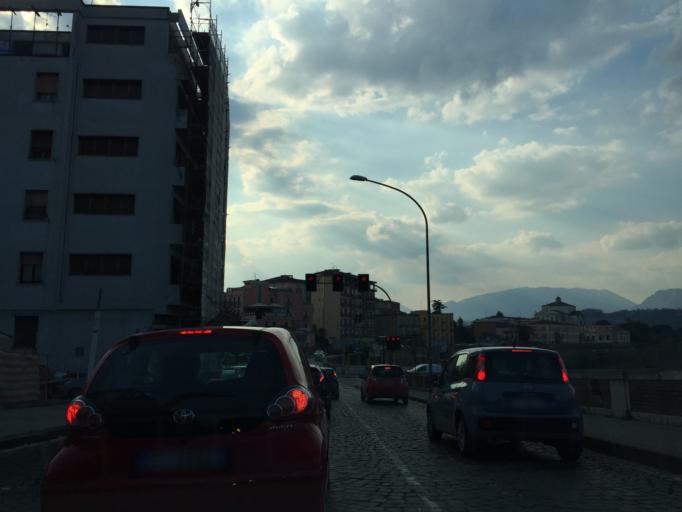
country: IT
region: Campania
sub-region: Provincia di Benevento
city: Benevento
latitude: 41.1336
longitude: 14.7745
